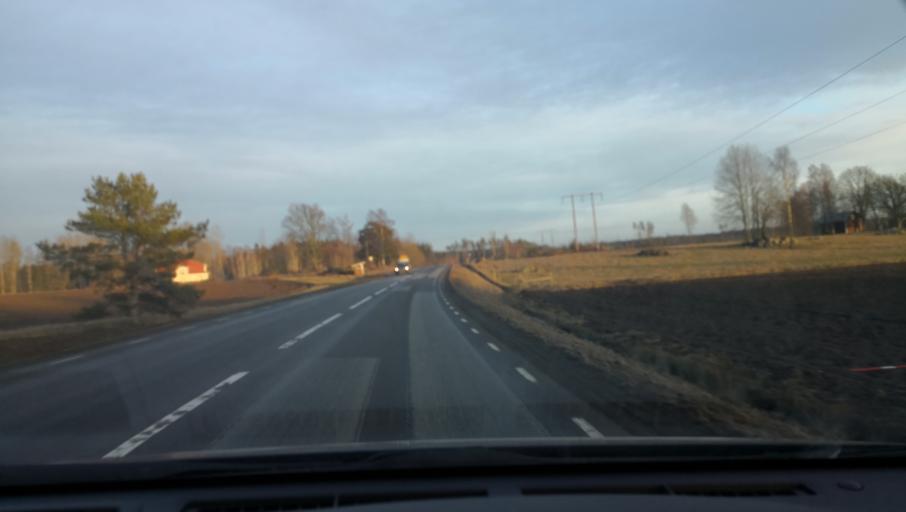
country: SE
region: OErebro
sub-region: Lekebergs Kommun
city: Fjugesta
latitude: 59.1639
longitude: 14.7391
